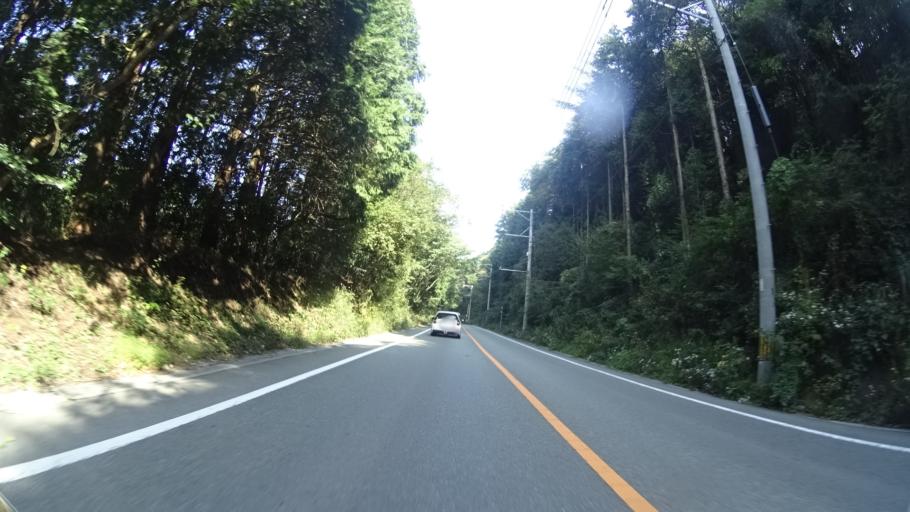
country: JP
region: Kumamoto
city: Ozu
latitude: 32.9021
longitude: 130.9405
